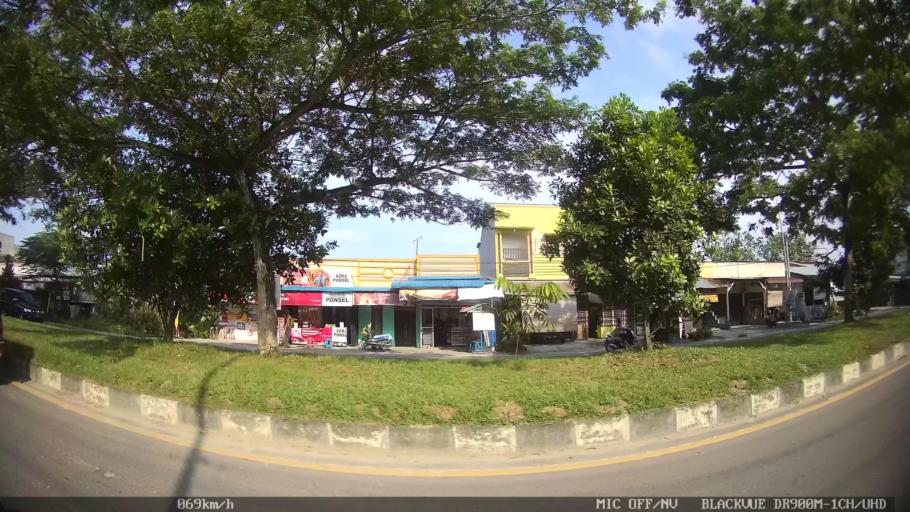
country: ID
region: North Sumatra
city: Percut
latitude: 3.5889
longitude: 98.8049
